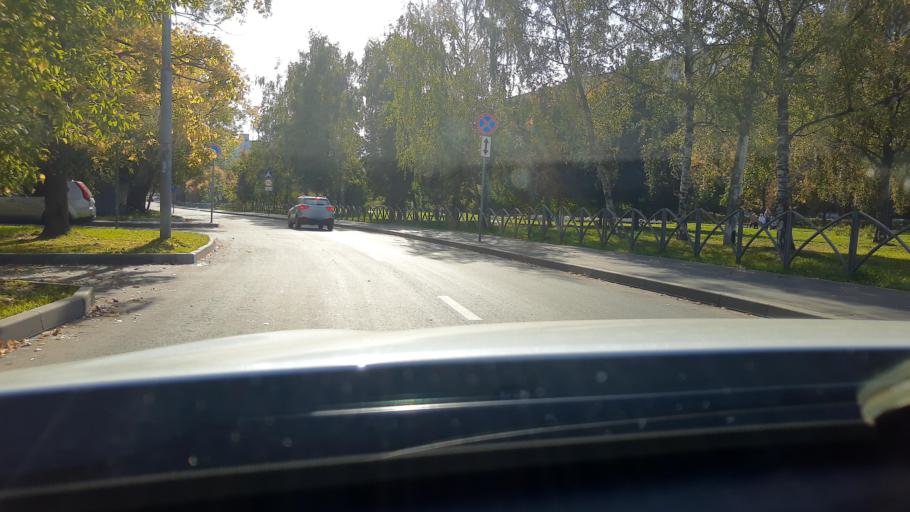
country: RU
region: Moscow
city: Vagonoremont
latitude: 55.8962
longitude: 37.5366
